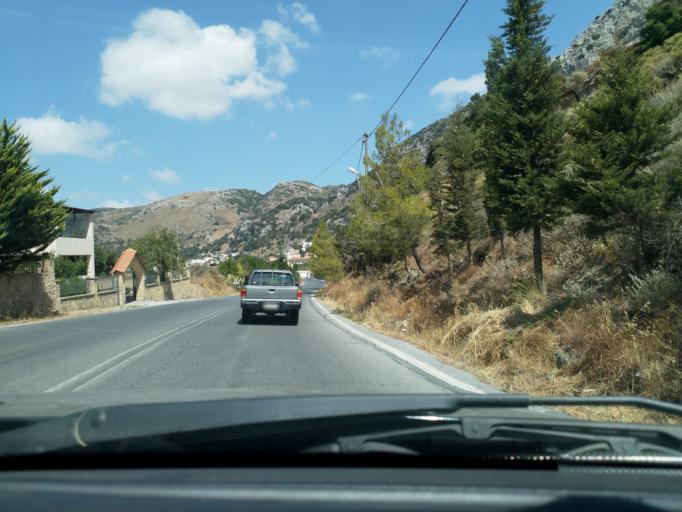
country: GR
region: Crete
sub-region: Nomos Rethymnis
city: Agia Foteini
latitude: 35.2096
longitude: 24.5344
